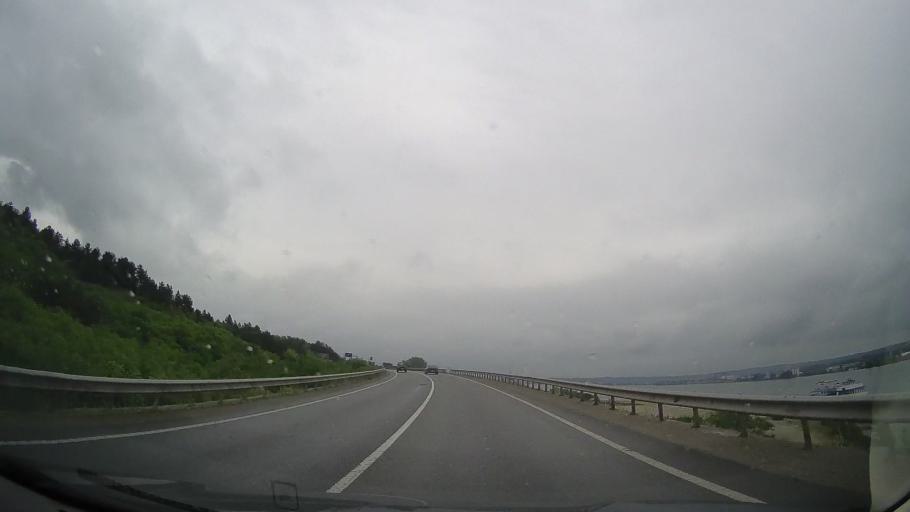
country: RO
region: Mehedinti
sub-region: Municipiul Drobeta-Turnu Severin
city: Gura Vaii
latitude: 44.6369
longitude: 22.5829
